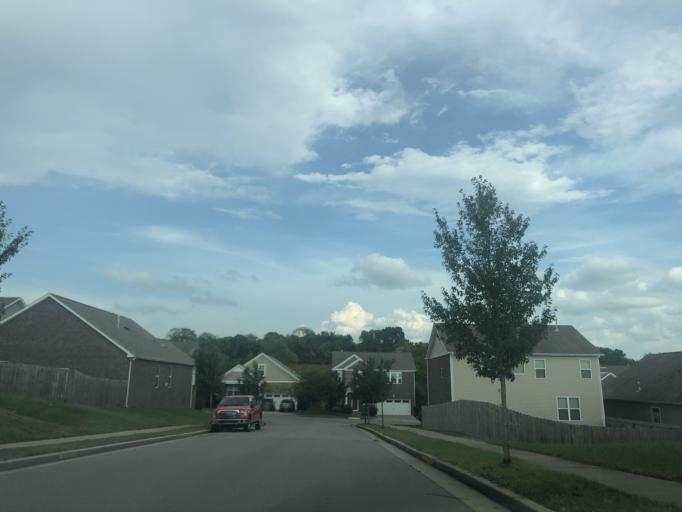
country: US
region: Tennessee
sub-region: Davidson County
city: Lakewood
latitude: 36.1651
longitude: -86.6205
